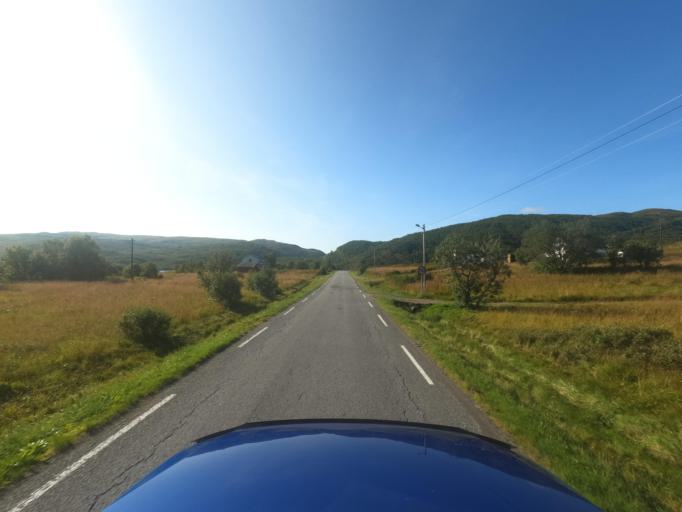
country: NO
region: Nordland
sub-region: Vestvagoy
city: Evjen
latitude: 68.3001
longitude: 13.8713
